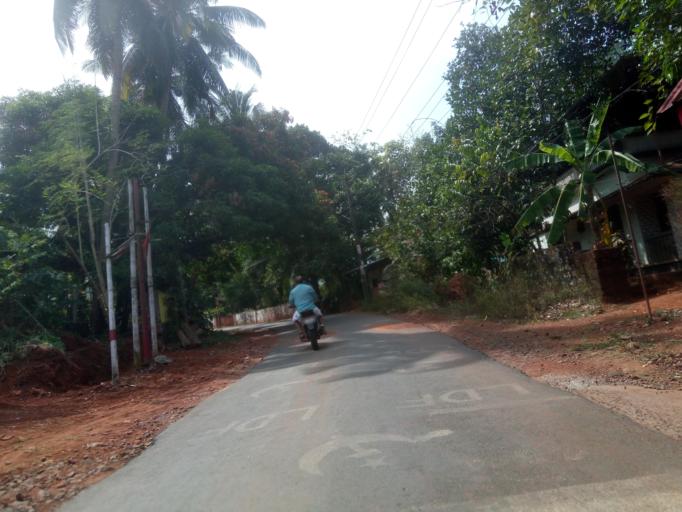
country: IN
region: Kerala
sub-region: Malappuram
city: Ponnani
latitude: 10.7930
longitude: 76.0289
